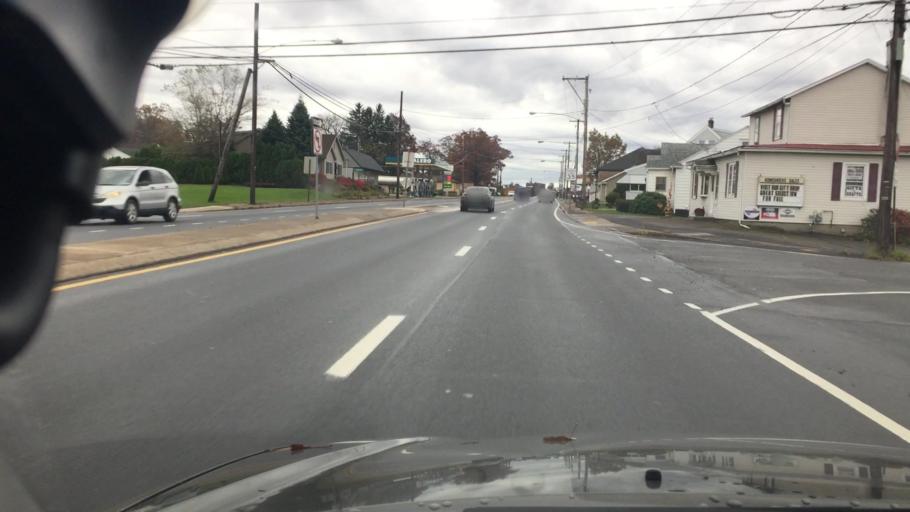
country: US
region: Pennsylvania
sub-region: Luzerne County
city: Harleigh
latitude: 40.9905
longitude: -75.9831
